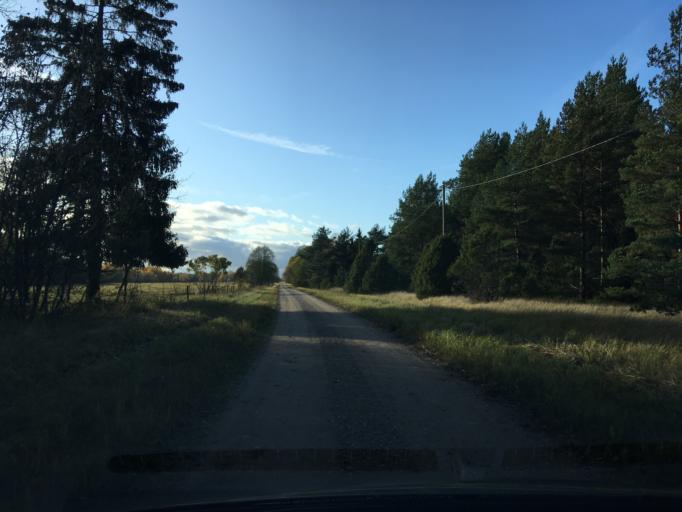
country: EE
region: Laeaene
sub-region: Lihula vald
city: Lihula
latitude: 58.5635
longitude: 23.8184
